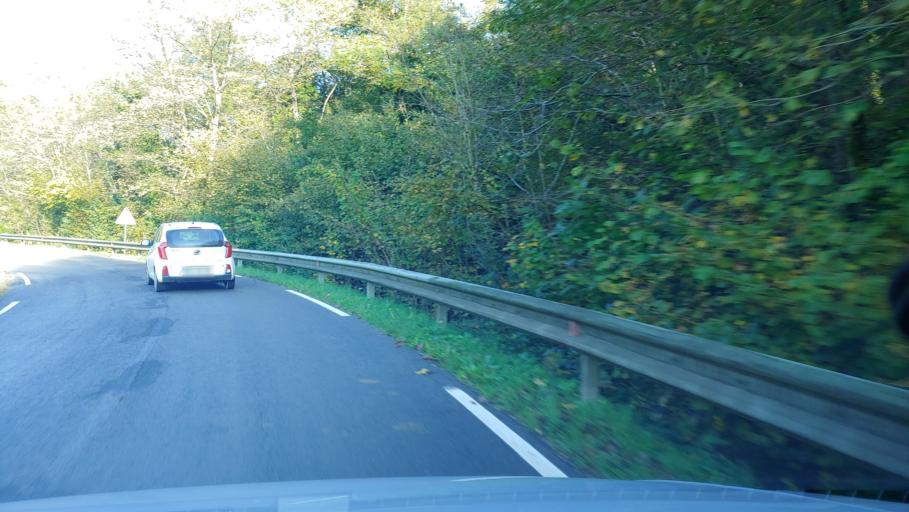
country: SI
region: Vipava
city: Vipava
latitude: 45.8127
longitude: 13.8986
